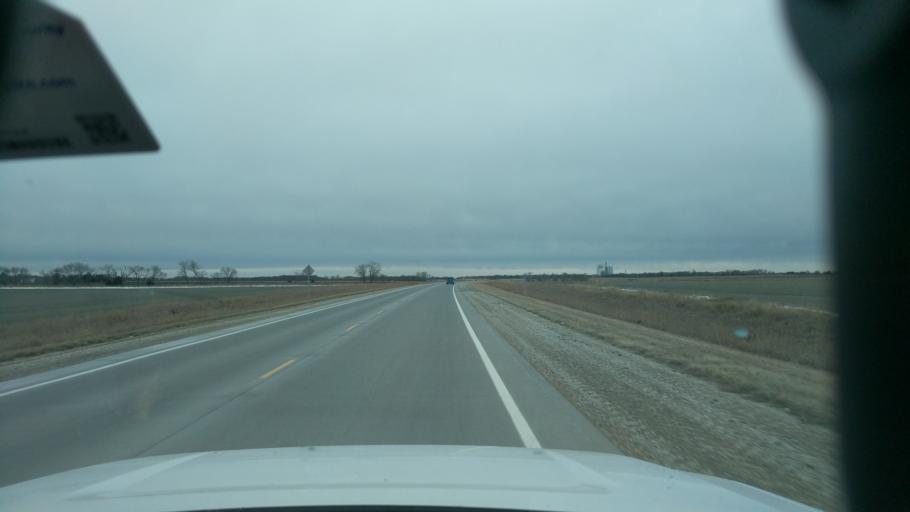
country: US
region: Kansas
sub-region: Dickinson County
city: Herington
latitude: 38.5181
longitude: -96.9563
